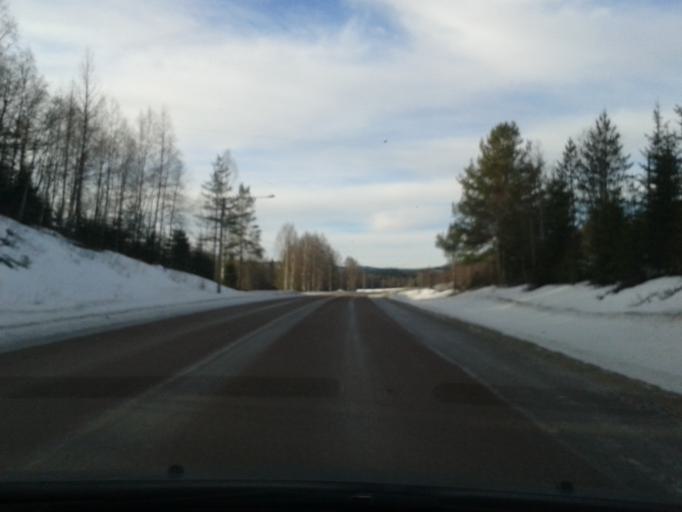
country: SE
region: Vaesternorrland
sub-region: OErnskoeldsviks Kommun
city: Bjasta
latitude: 63.3898
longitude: 18.3521
